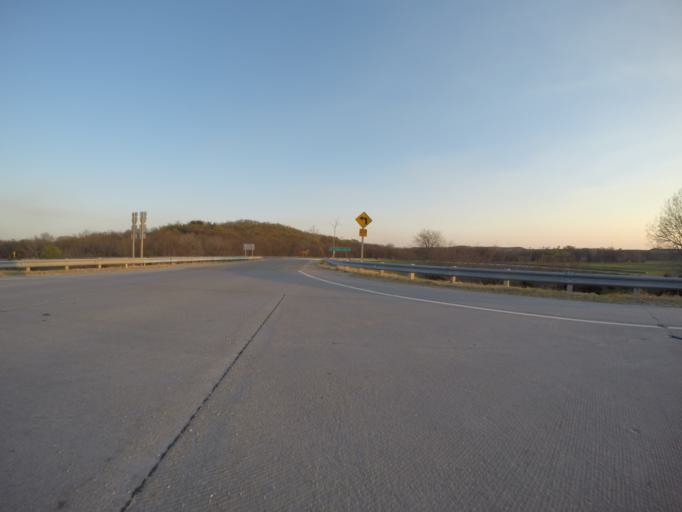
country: US
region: Kansas
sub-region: Riley County
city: Ogden
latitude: 39.0660
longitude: -96.6572
